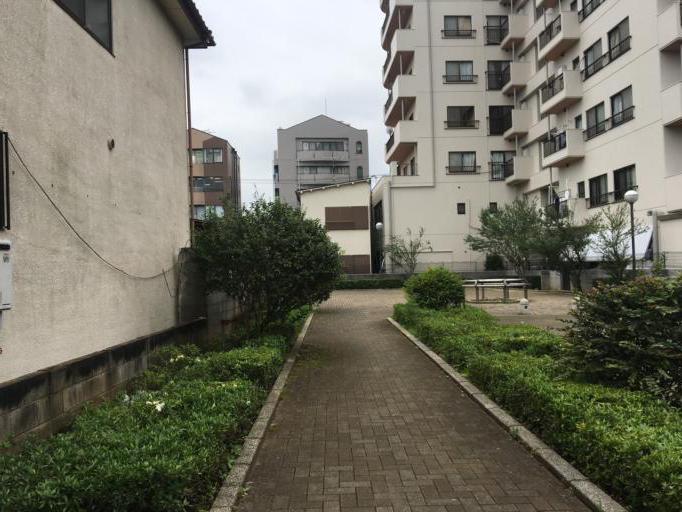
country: JP
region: Saitama
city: Ageoshimo
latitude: 35.9712
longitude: 139.5940
